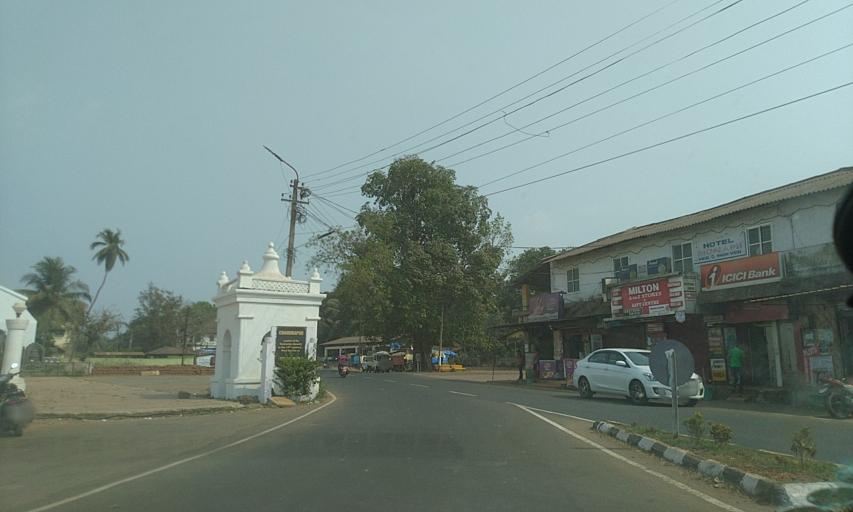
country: IN
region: Goa
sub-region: South Goa
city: Davorlim
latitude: 15.2615
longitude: 74.0444
